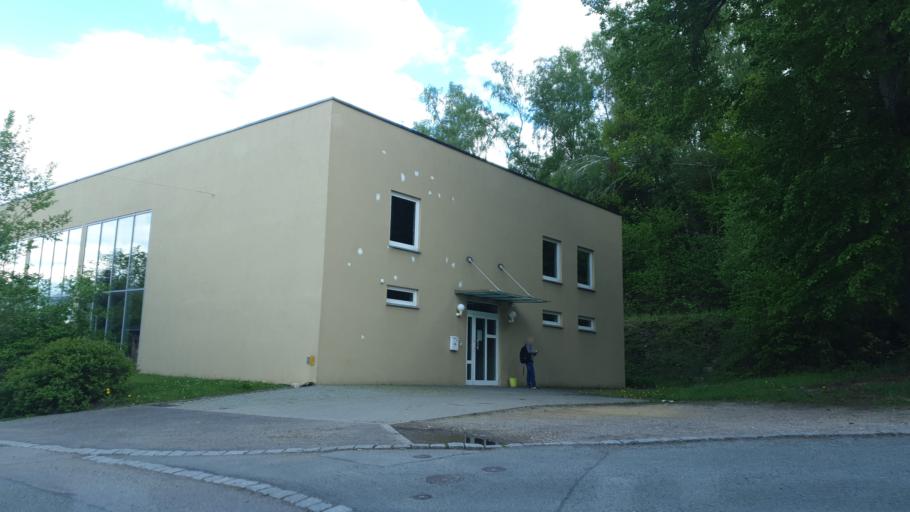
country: DE
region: Saxony
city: Oelsnitz
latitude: 50.7264
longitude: 12.6929
